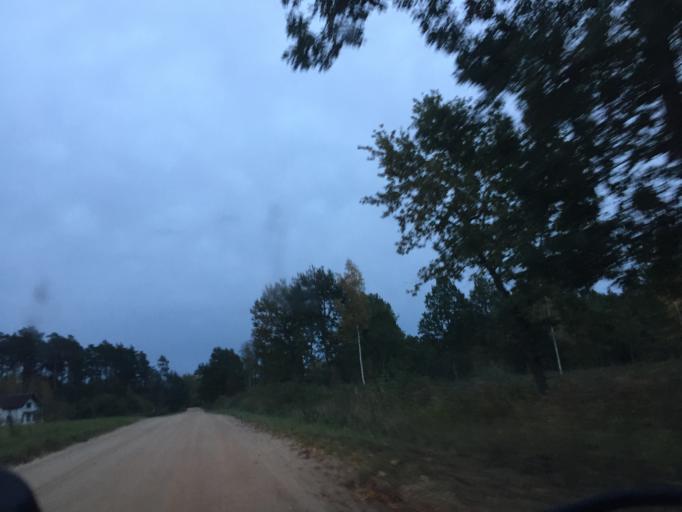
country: LV
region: Adazi
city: Adazi
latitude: 57.0840
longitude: 24.3602
